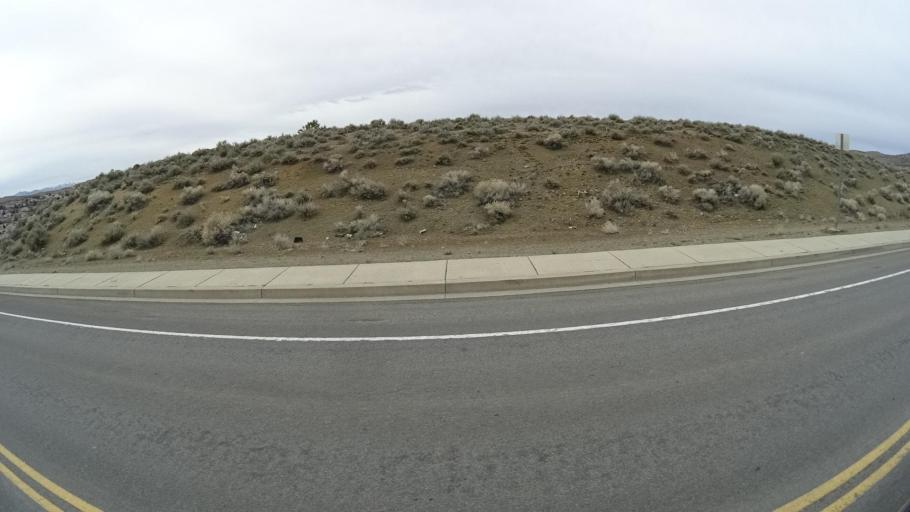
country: US
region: Nevada
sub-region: Washoe County
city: Sun Valley
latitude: 39.6095
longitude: -119.7600
